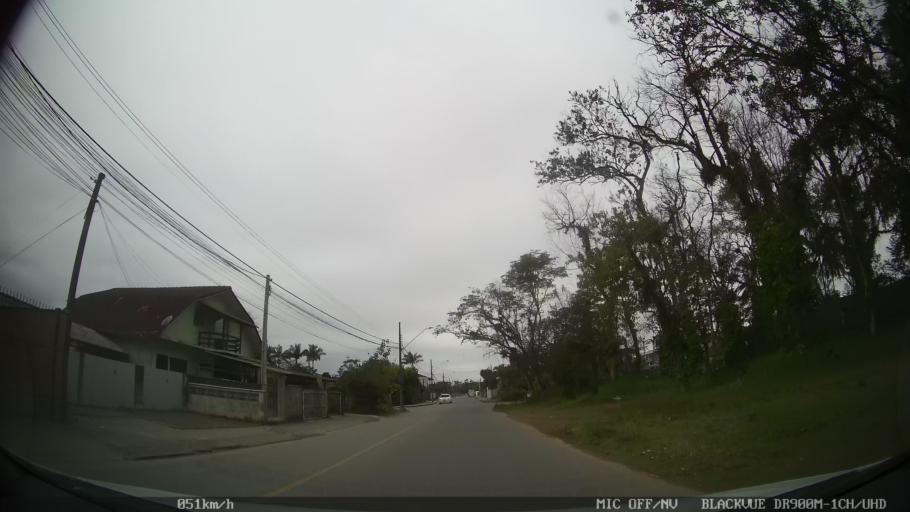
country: BR
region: Santa Catarina
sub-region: Joinville
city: Joinville
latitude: -26.2937
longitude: -48.9097
